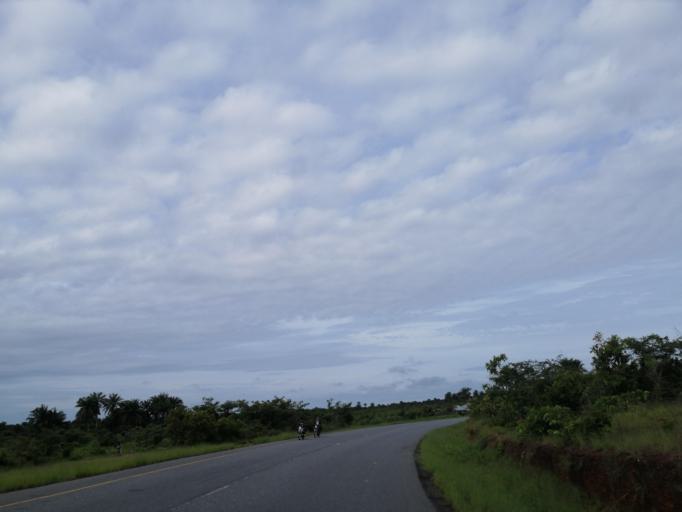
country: SL
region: Northern Province
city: Port Loko
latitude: 8.7749
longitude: -12.8574
